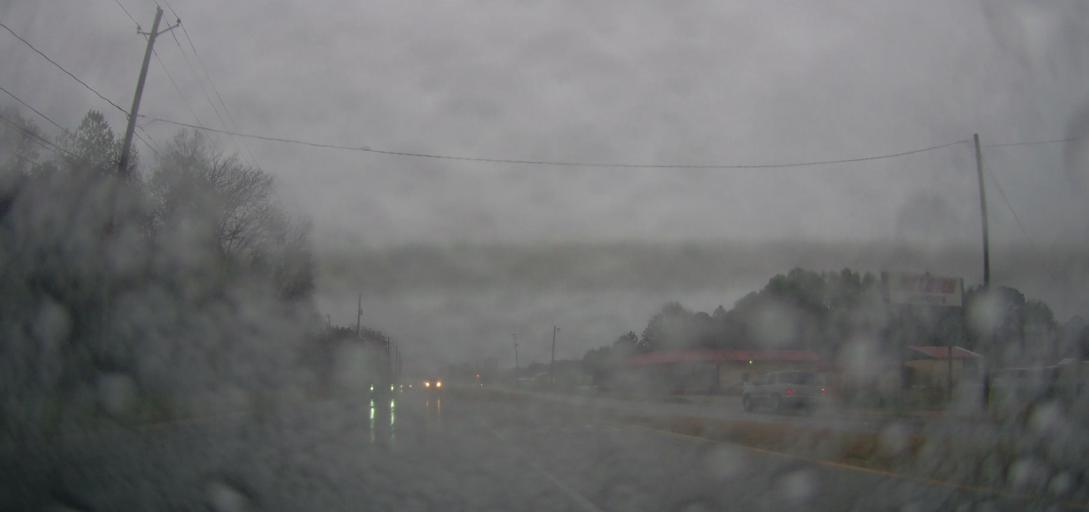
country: US
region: Alabama
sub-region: Autauga County
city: Prattville
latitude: 32.4018
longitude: -86.4017
